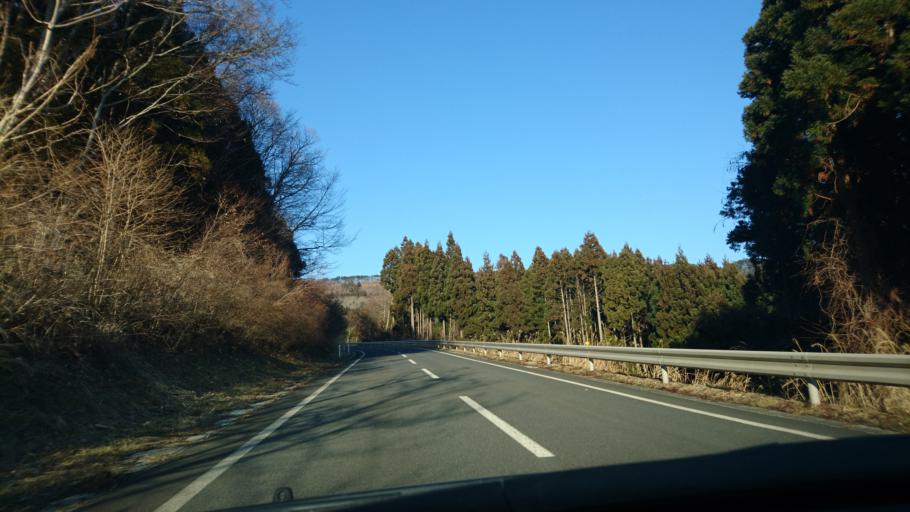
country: JP
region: Iwate
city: Ichinoseki
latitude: 38.8550
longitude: 141.3899
